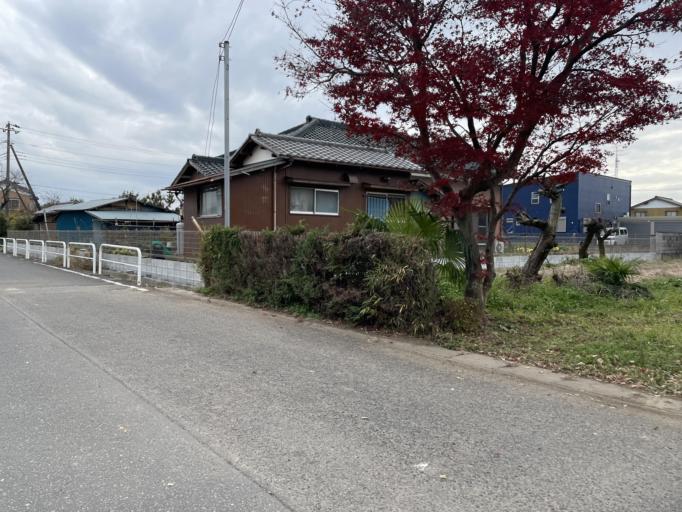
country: JP
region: Saitama
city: Shiraoka
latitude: 36.0299
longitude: 139.6380
